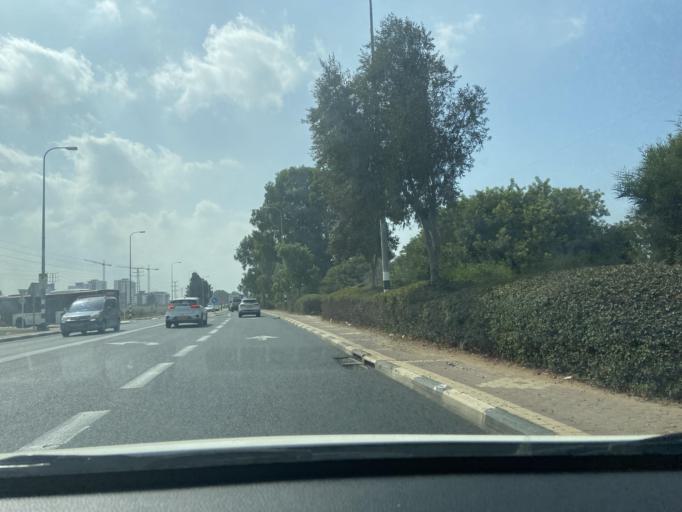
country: IL
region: Northern District
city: Nahariya
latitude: 33.0242
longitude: 35.1036
